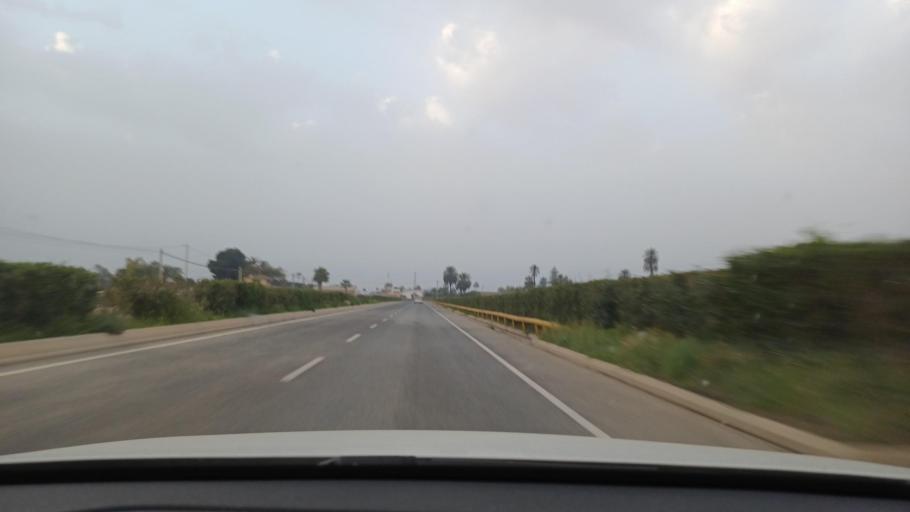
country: ES
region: Valencia
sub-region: Provincia de Alicante
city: Elche
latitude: 38.2283
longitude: -0.6994
